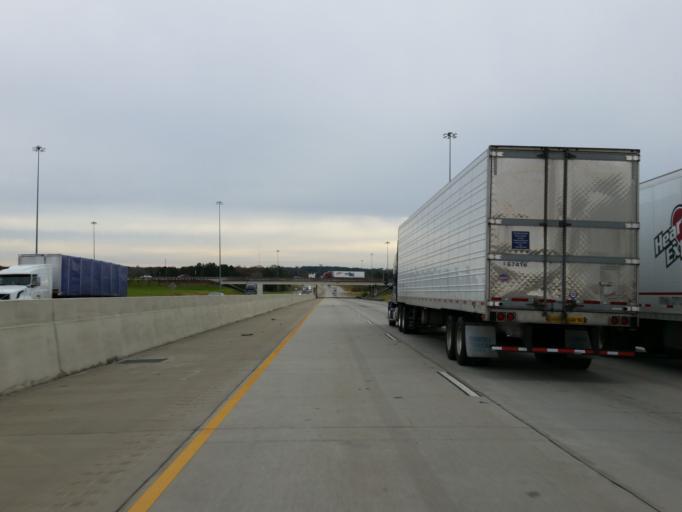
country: US
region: Georgia
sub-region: Crisp County
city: Cordele
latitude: 31.9373
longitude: -83.7480
